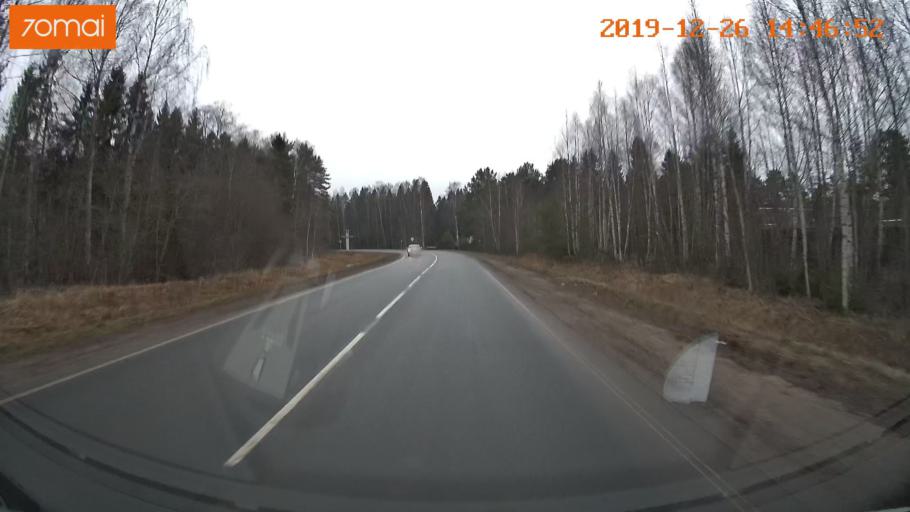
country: RU
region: Jaroslavl
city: Poshekhon'ye
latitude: 58.3402
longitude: 39.0105
